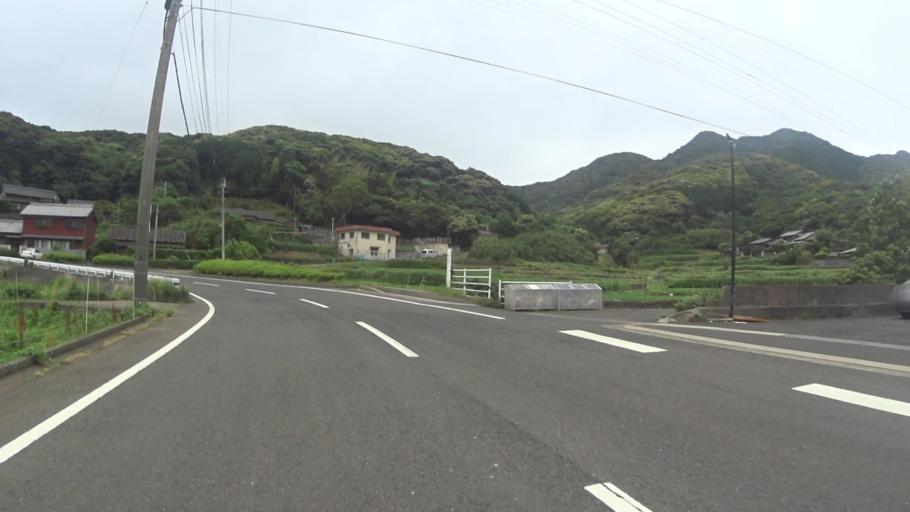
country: JP
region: Nagasaki
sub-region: Hirado Shi
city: Hirado
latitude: 33.1857
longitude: 129.3651
